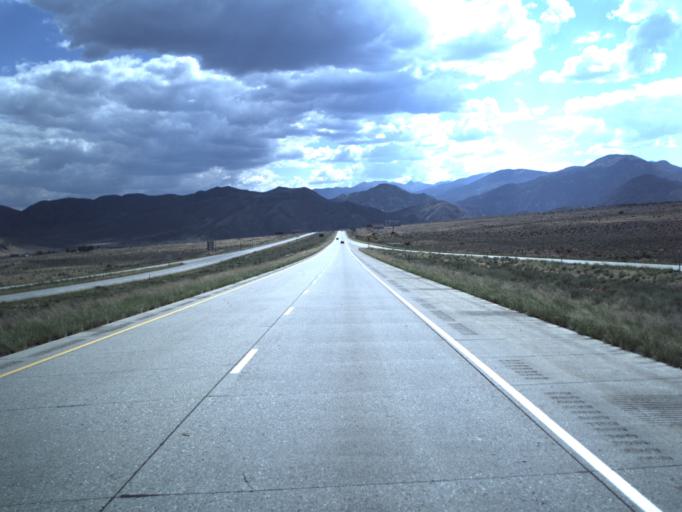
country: US
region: Utah
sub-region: Sevier County
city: Monroe
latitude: 38.6226
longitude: -112.2275
